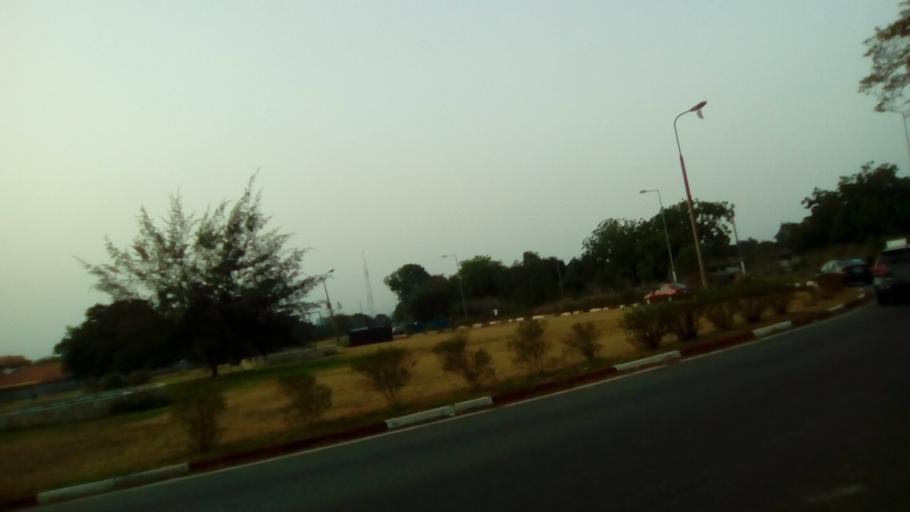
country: GH
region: Greater Accra
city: Medina Estates
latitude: 5.6403
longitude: -0.1838
